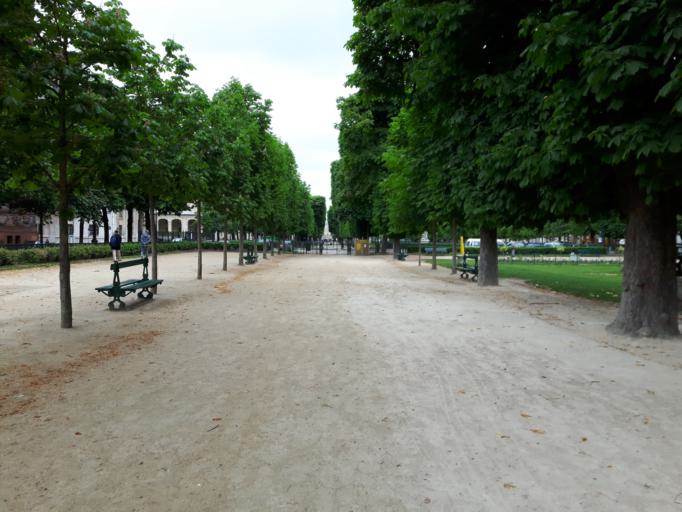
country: FR
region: Ile-de-France
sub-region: Paris
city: Paris
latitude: 48.8420
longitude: 2.3365
